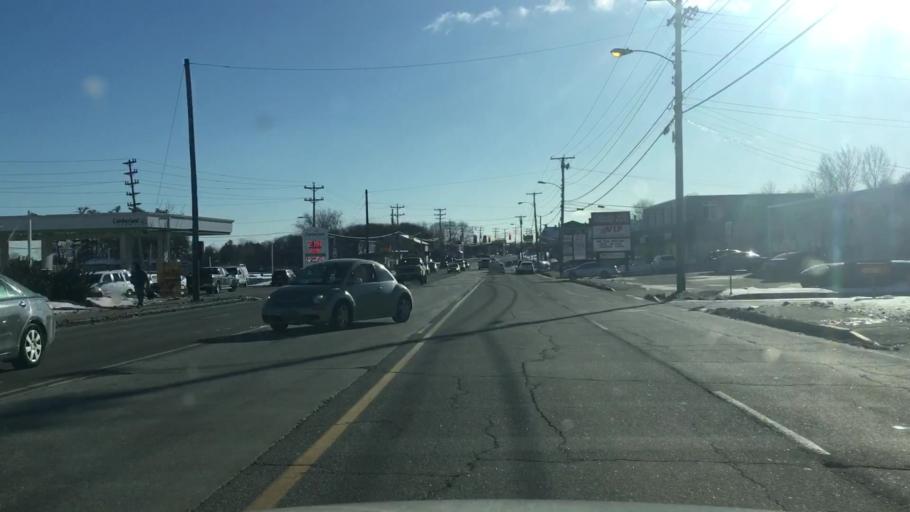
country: US
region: Maine
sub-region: Androscoggin County
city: Auburn
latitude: 44.1072
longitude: -70.2259
